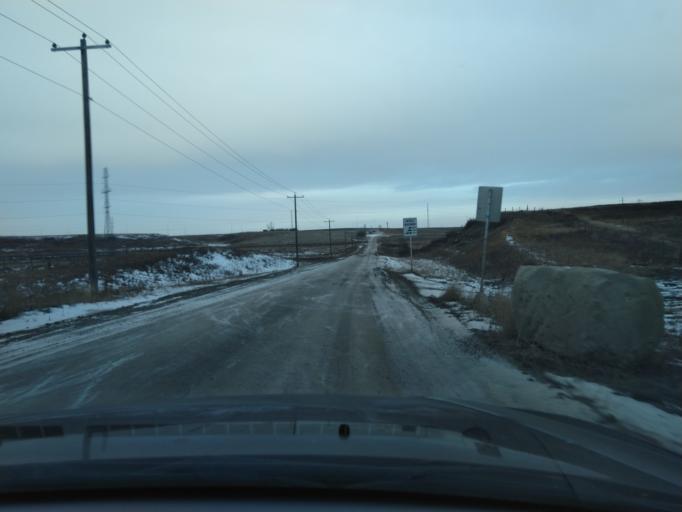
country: CA
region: Alberta
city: Airdrie
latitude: 51.1691
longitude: -114.0249
